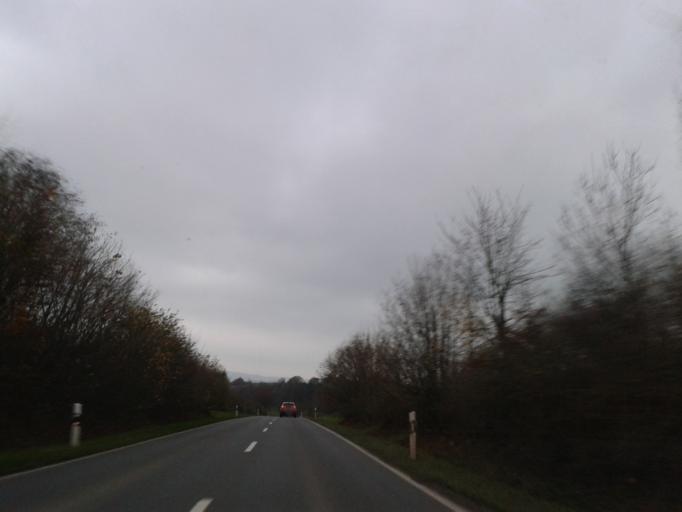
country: DE
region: North Rhine-Westphalia
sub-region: Regierungsbezirk Detmold
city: Blomberg
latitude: 51.9358
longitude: 9.1317
